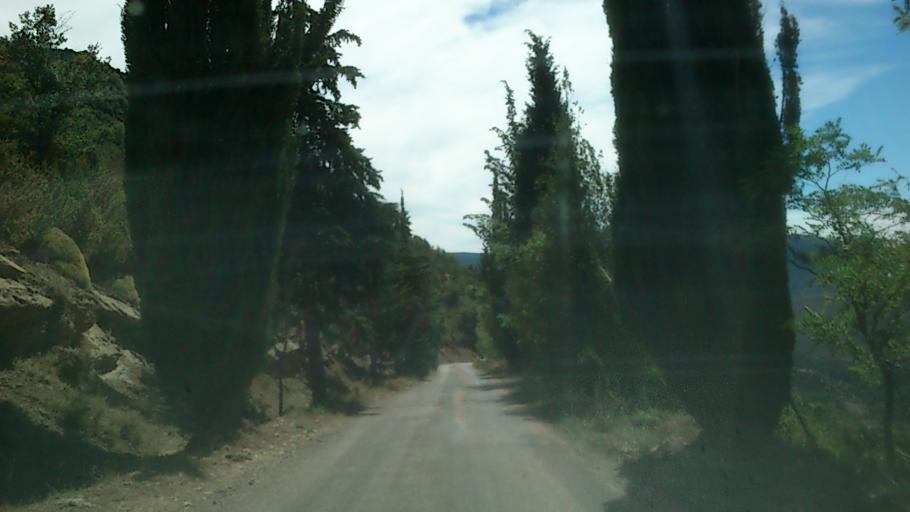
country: ES
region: Aragon
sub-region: Provincia de Huesca
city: Arguis
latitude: 42.3273
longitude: -0.4016
